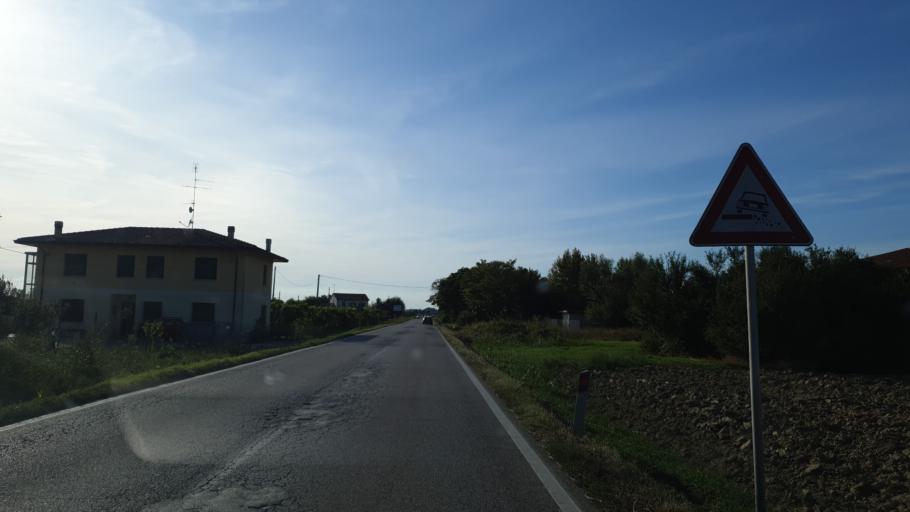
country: IT
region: Emilia-Romagna
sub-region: Provincia di Ravenna
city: Voltana
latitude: 44.5481
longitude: 11.9630
